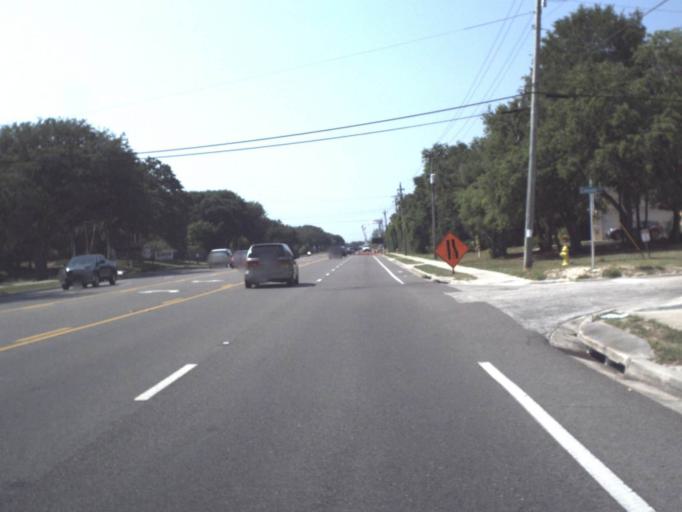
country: US
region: Florida
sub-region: Saint Johns County
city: Saint Augustine Beach
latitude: 29.8739
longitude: -81.2849
